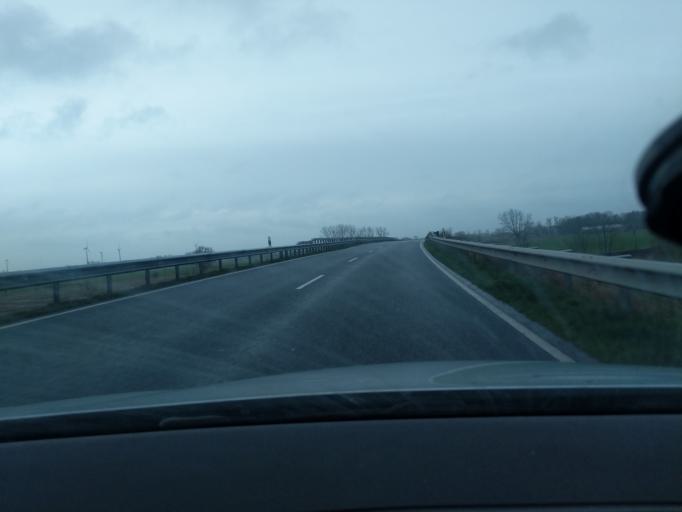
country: DE
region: Lower Saxony
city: Otterndorf
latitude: 53.8043
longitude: 8.9237
